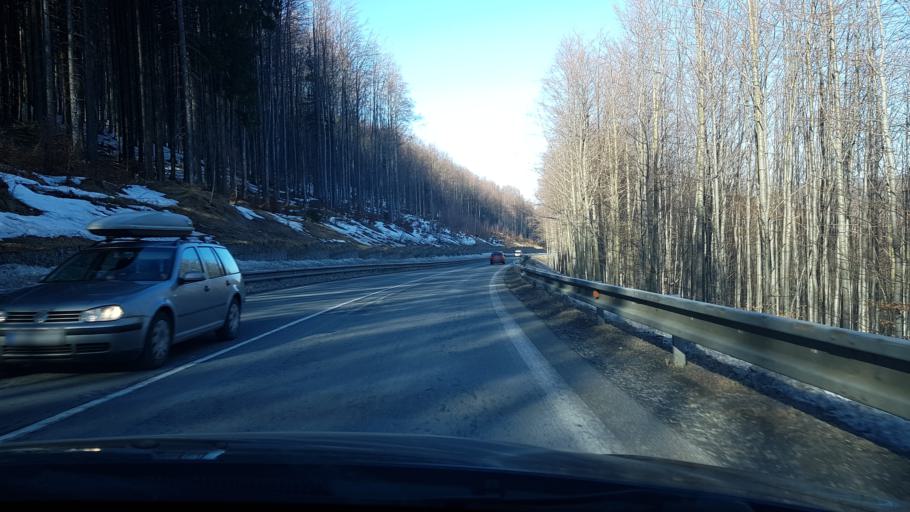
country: CZ
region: Olomoucky
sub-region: Okres Jesenik
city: Jesenik
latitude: 50.1434
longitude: 17.1659
